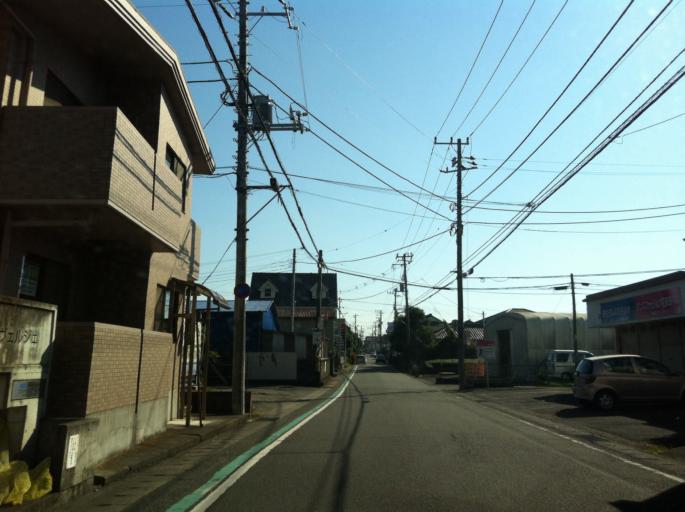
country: JP
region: Shizuoka
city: Fuji
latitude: 35.1487
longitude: 138.7754
